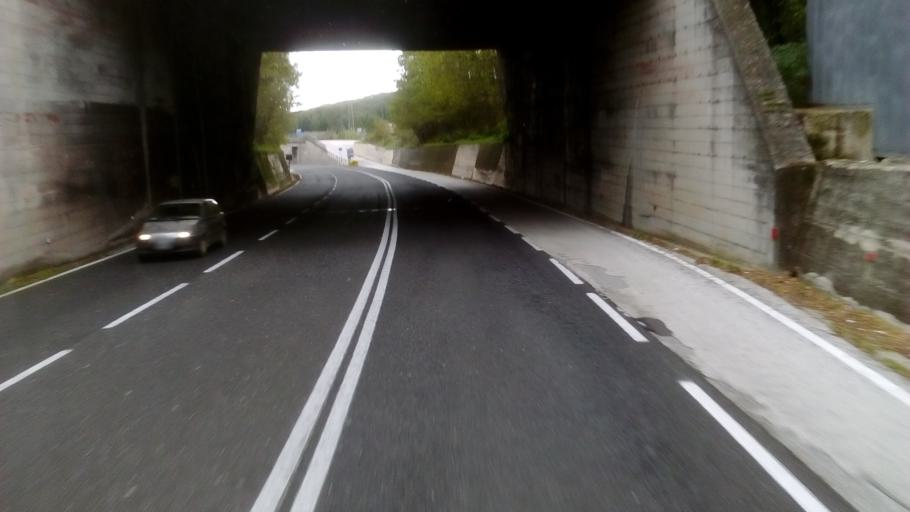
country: IT
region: Molise
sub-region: Provincia di Isernia
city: Isernia
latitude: 41.5910
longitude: 14.2418
